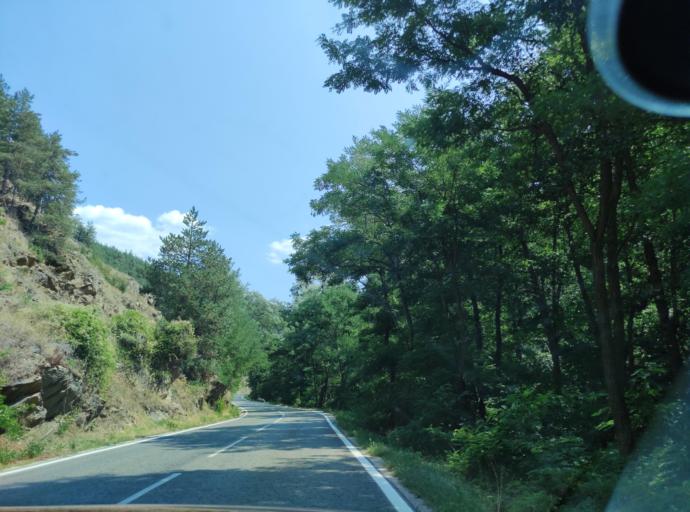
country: BG
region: Blagoevgrad
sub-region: Obshtina Belitsa
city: Belitsa
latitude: 41.8930
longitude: 23.5502
